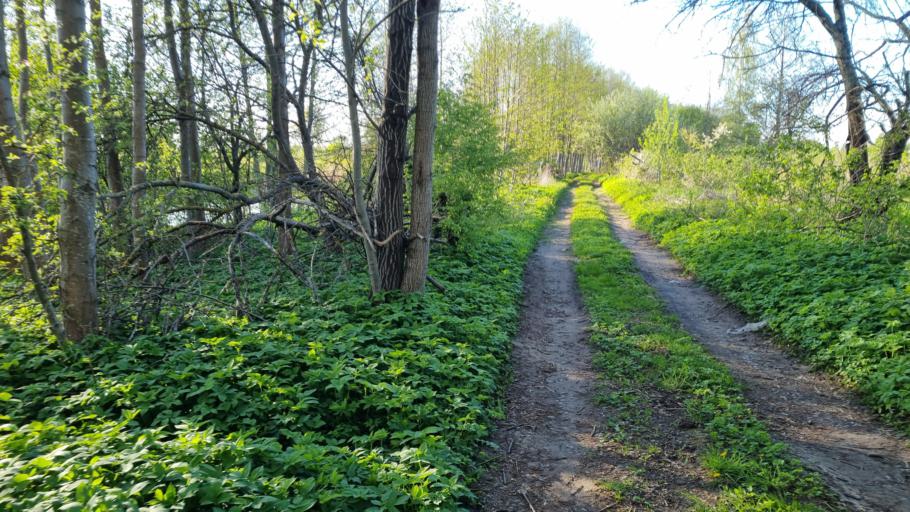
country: LV
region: Riga
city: Bolderaja
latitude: 56.9850
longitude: 24.0598
